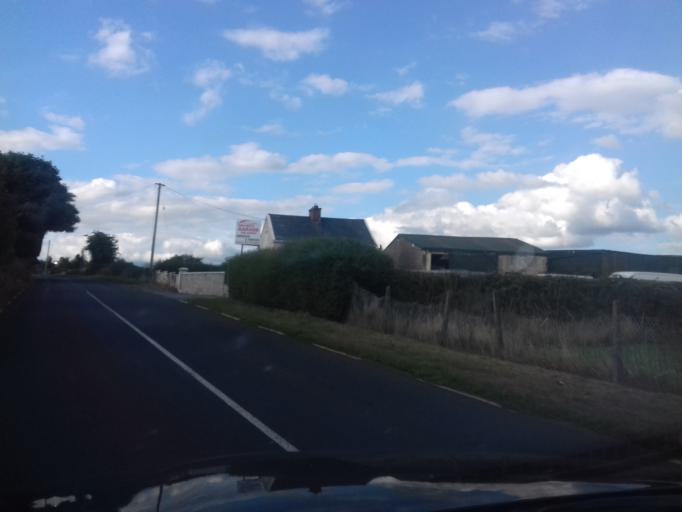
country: IE
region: Leinster
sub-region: Loch Garman
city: New Ross
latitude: 52.4399
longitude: -6.9606
